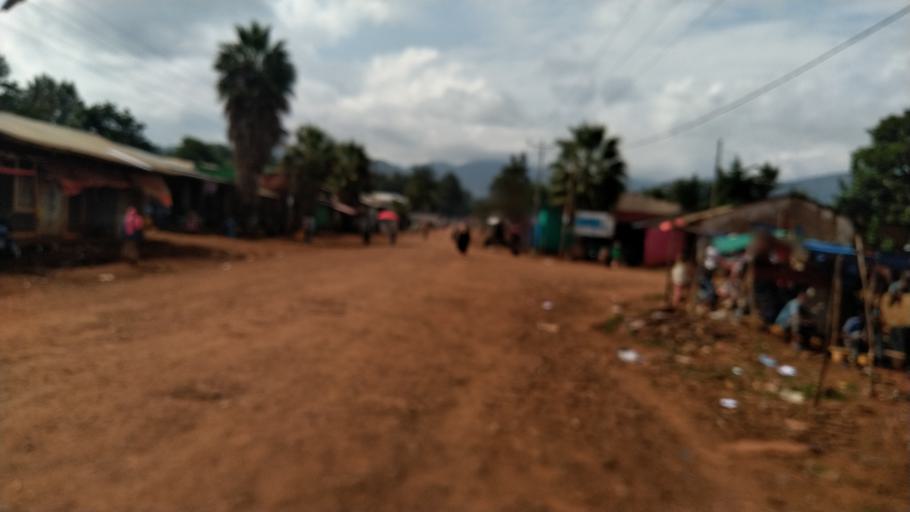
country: ET
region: Oromiya
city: Jima
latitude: 7.6318
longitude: 37.2524
